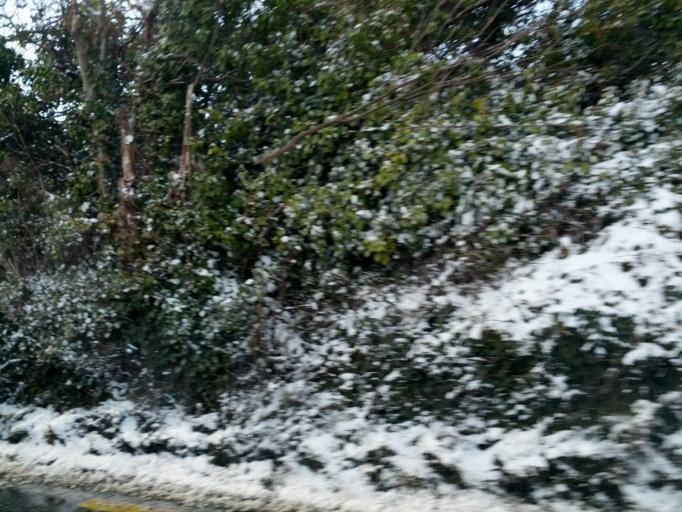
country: IE
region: Connaught
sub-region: County Galway
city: Athenry
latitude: 53.2254
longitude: -8.7384
